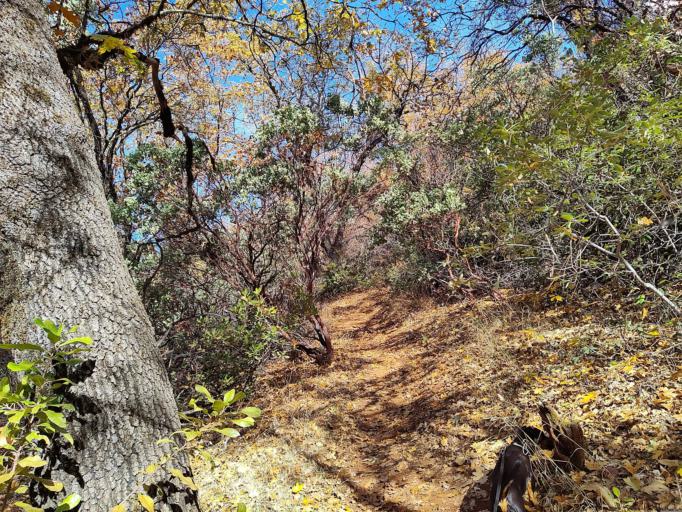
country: US
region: California
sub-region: Placer County
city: Meadow Vista
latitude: 39.0259
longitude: -120.9822
